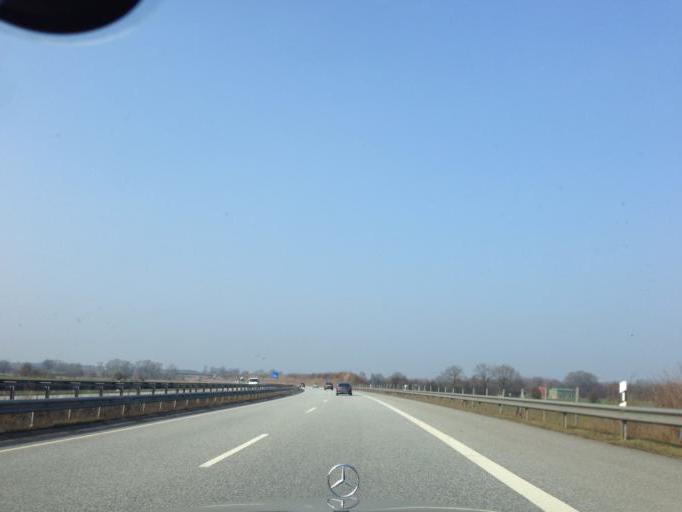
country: DE
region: Schleswig-Holstein
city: Daldorf
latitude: 54.0056
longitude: 10.2526
